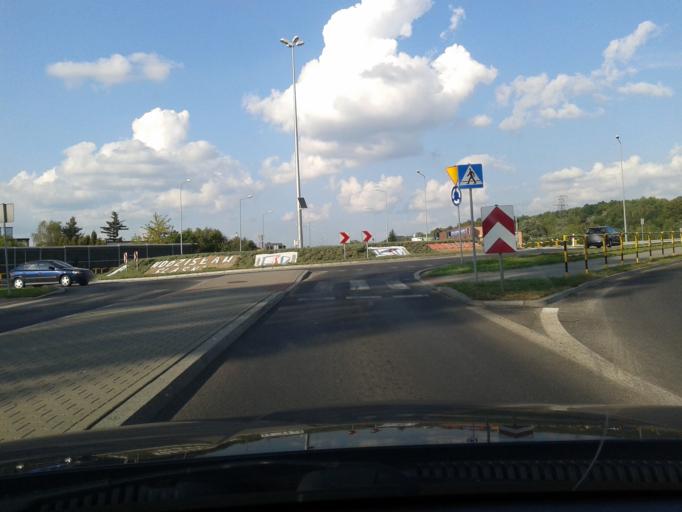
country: PL
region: Silesian Voivodeship
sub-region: Powiat wodzislawski
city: Wodzislaw Slaski
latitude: 50.0123
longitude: 18.4748
